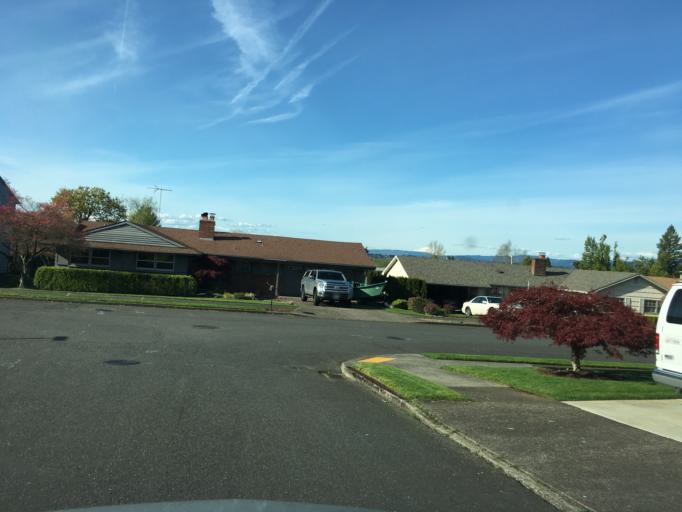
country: US
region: Oregon
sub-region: Multnomah County
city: Lents
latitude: 45.5472
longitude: -122.5200
